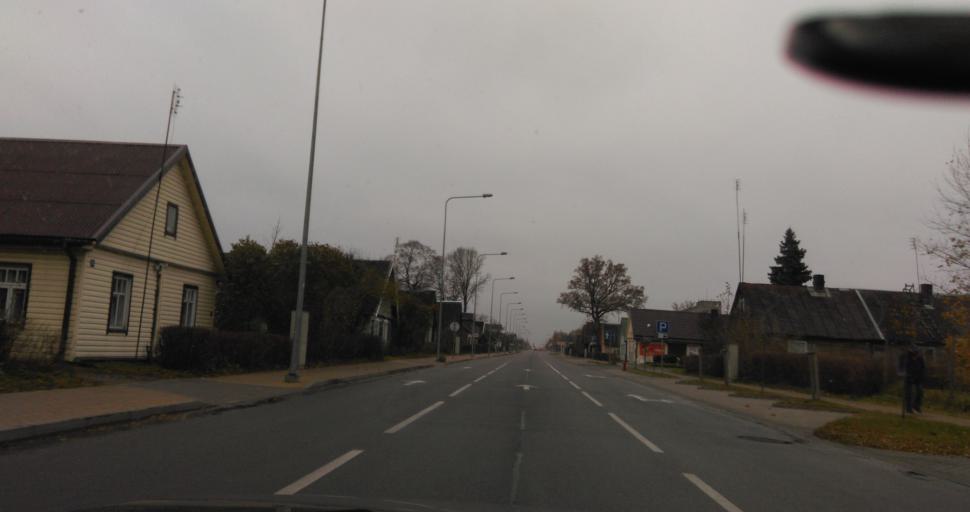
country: LT
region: Panevezys
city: Rokiskis
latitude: 55.9585
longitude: 25.5876
